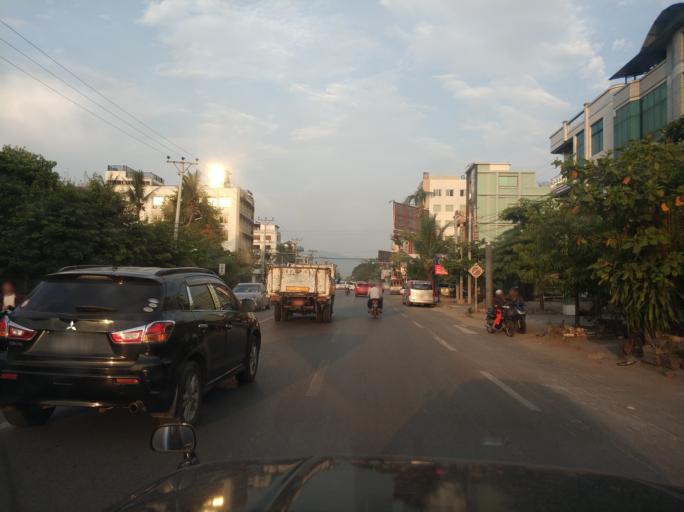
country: MM
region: Mandalay
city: Mandalay
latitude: 21.9681
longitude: 96.1004
